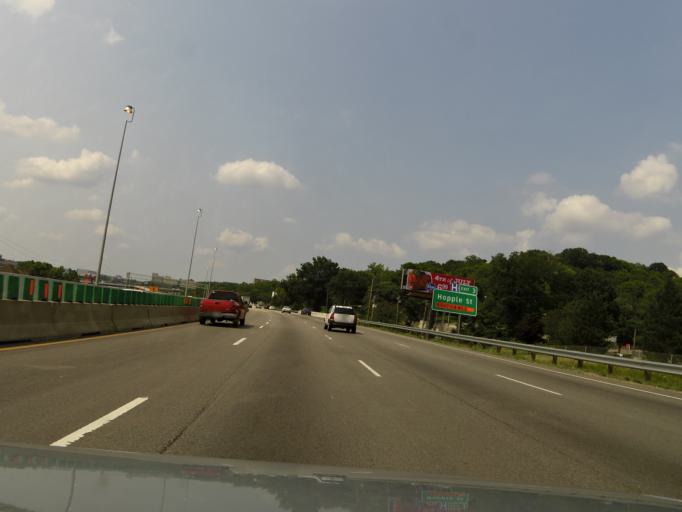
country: US
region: Kentucky
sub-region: Kenton County
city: Ludlow
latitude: 39.1310
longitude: -84.5326
